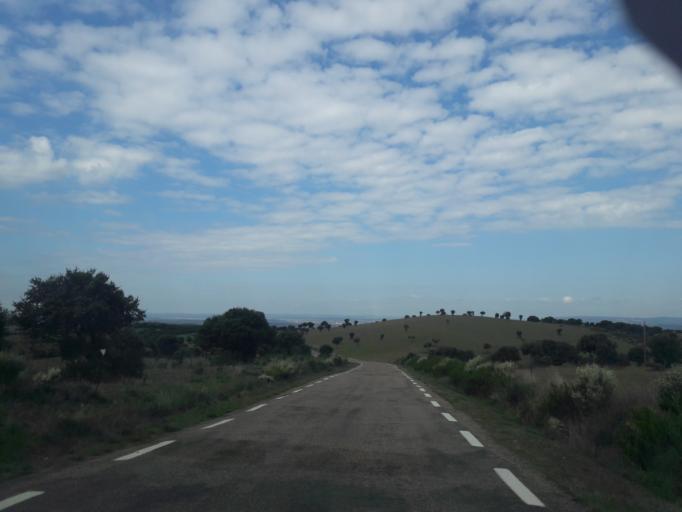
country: ES
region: Castille and Leon
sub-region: Provincia de Salamanca
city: Zamarra
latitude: 40.5430
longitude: -6.4070
